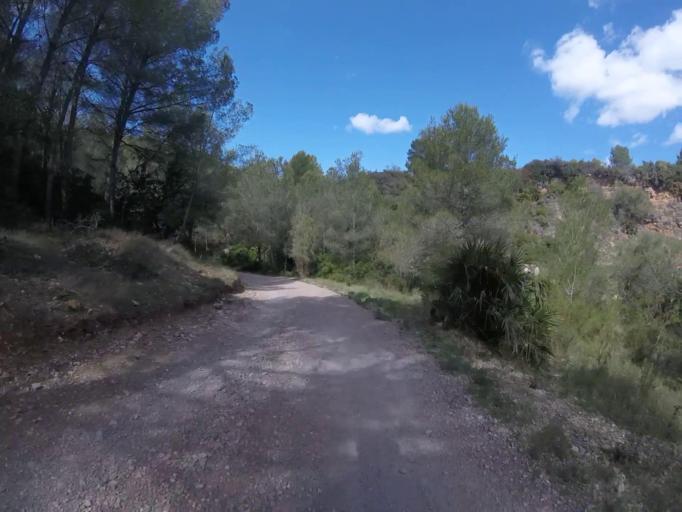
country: ES
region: Valencia
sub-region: Provincia de Castello
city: Santa Magdalena de Pulpis
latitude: 40.3181
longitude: 0.3308
